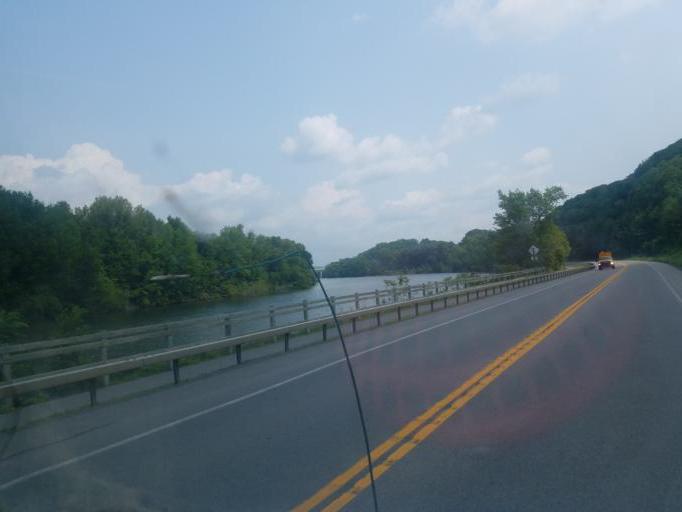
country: US
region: New York
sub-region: Herkimer County
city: Herkimer
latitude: 43.0137
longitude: -74.9911
